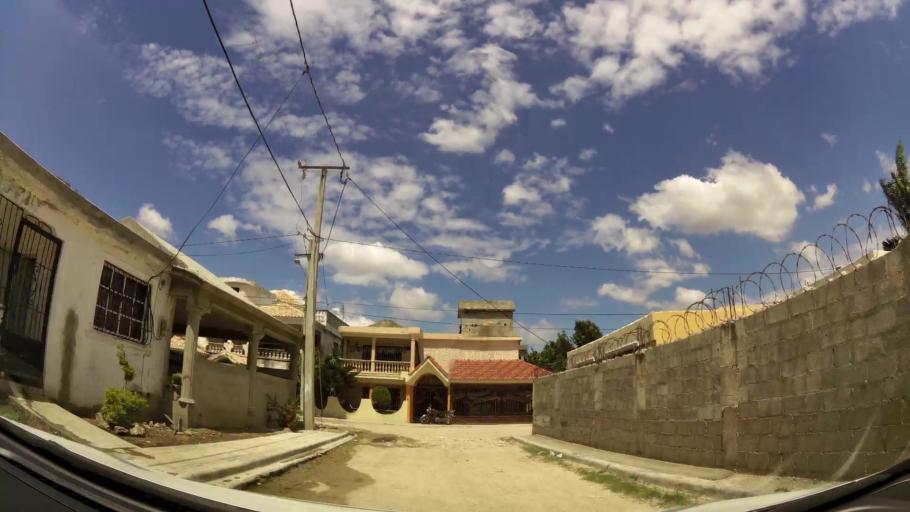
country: DO
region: San Cristobal
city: San Cristobal
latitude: 18.4095
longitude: -70.1009
